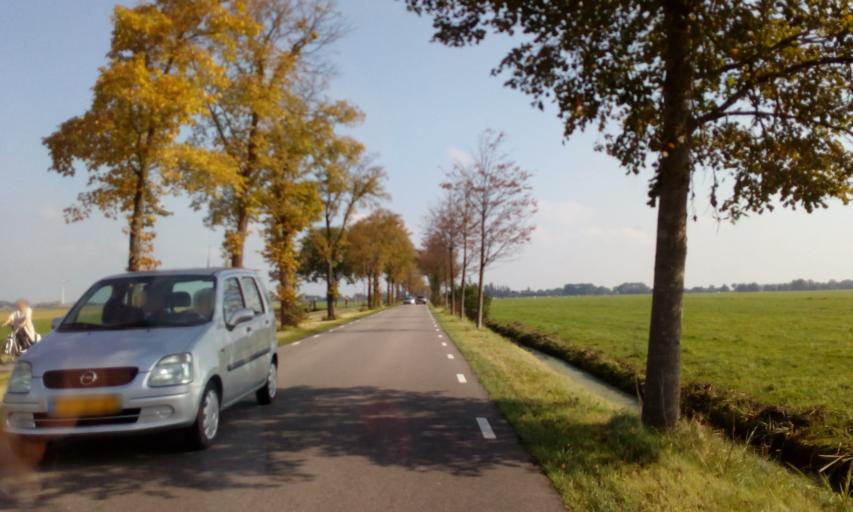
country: NL
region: South Holland
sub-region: Gemeente Leiden
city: Leiden
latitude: 52.1187
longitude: 4.5088
